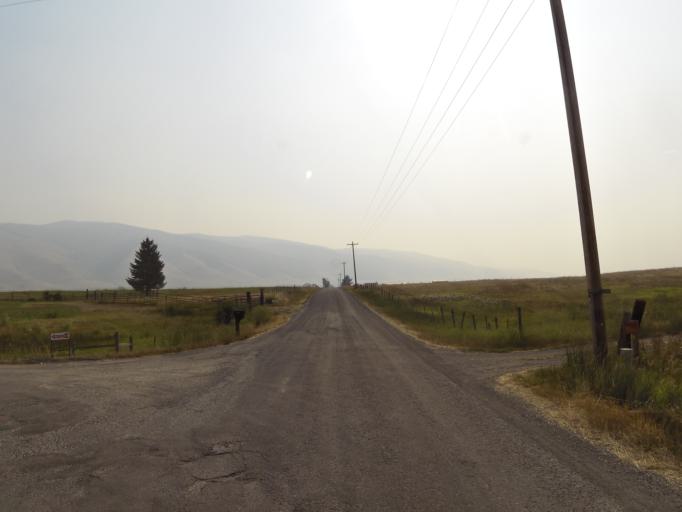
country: US
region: Montana
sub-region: Missoula County
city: Frenchtown
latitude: 47.1890
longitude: -114.0971
